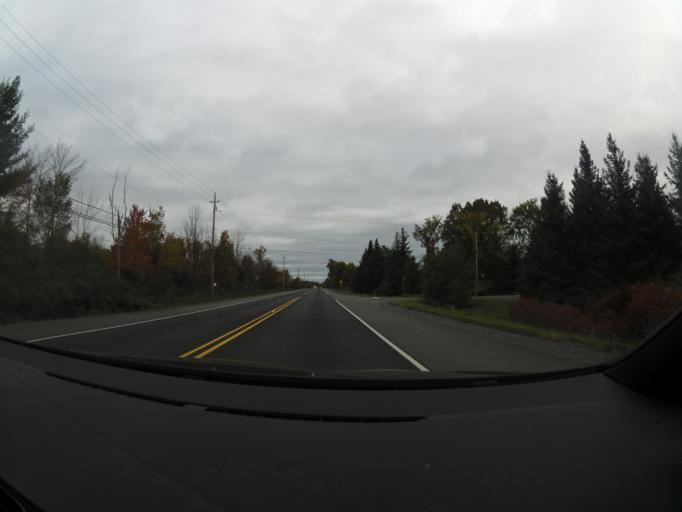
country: CA
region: Ontario
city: Bells Corners
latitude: 45.3898
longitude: -75.9794
